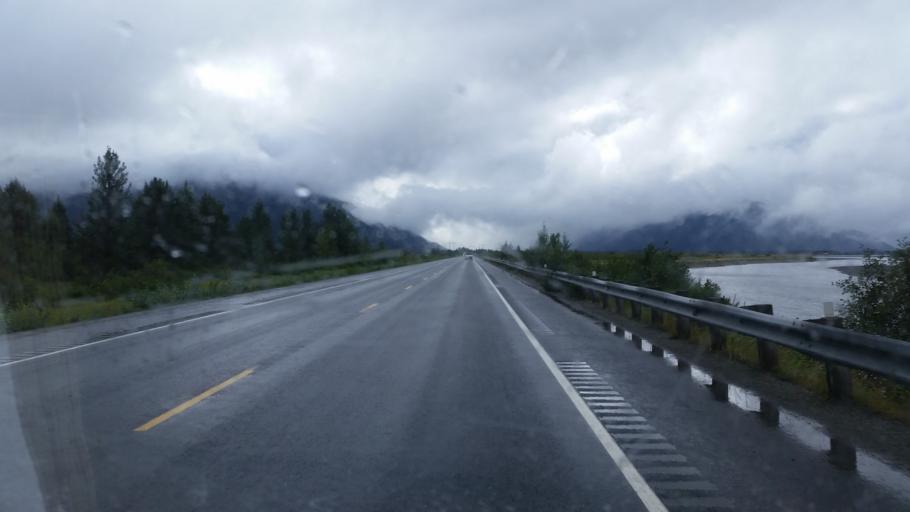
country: US
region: Alaska
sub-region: Anchorage Municipality
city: Girdwood
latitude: 60.8566
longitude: -149.0121
